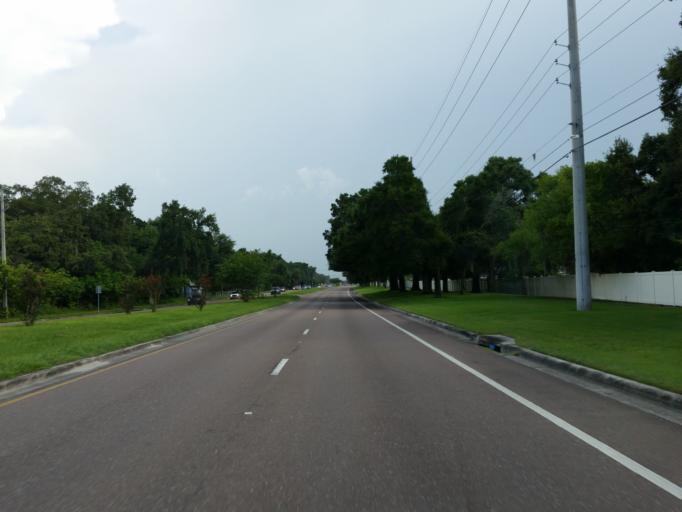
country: US
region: Florida
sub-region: Hillsborough County
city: Riverview
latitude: 27.9059
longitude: -82.3187
